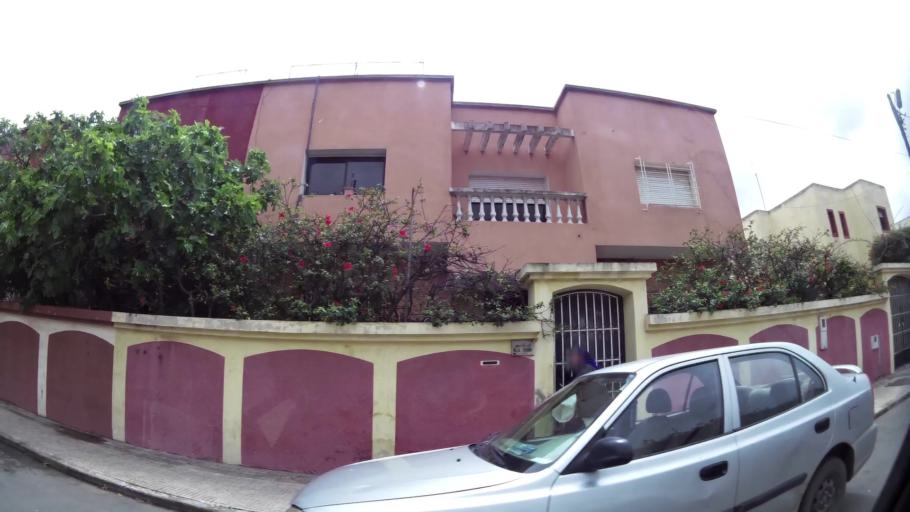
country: MA
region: Grand Casablanca
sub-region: Mediouna
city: Tit Mellil
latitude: 33.6133
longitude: -7.5225
